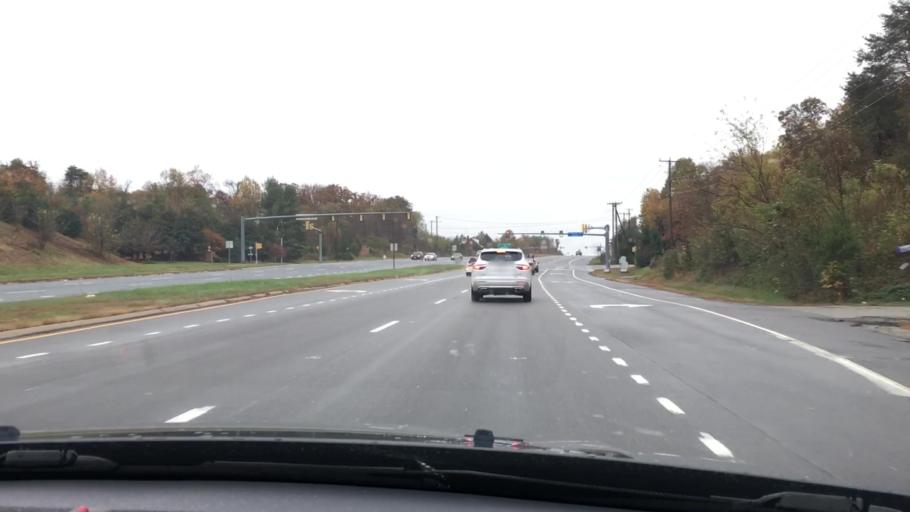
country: US
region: Virginia
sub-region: Fairfax County
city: Lorton
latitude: 38.7125
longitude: -77.2629
